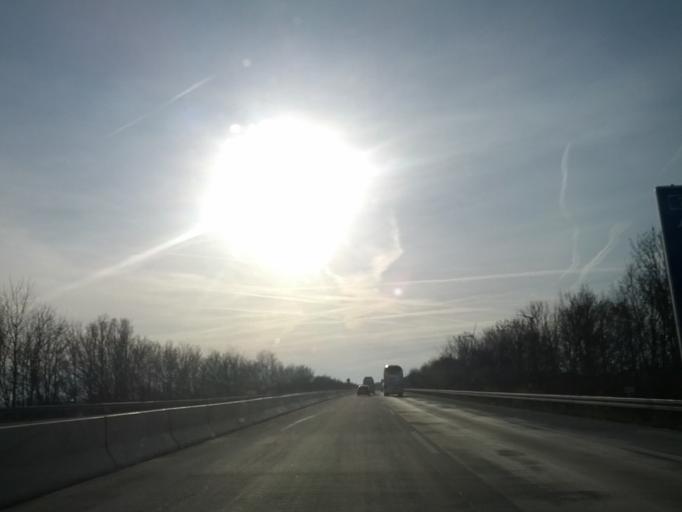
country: DE
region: Bavaria
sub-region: Regierungsbezirk Mittelfranken
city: Gollhofen
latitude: 49.5940
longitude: 10.1743
